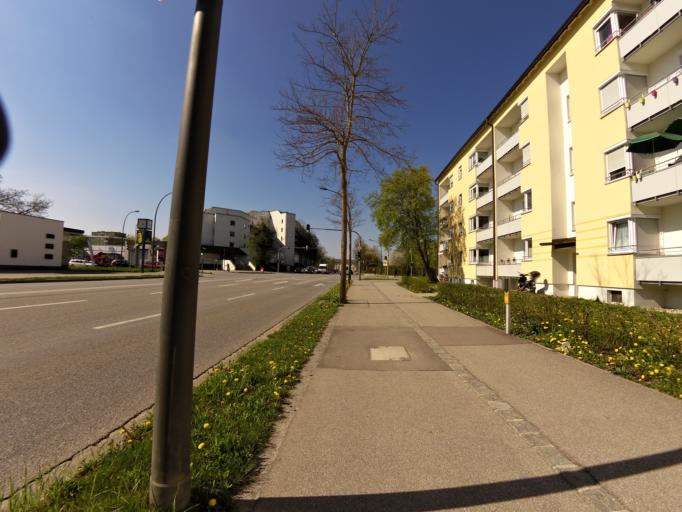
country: DE
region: Bavaria
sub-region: Lower Bavaria
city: Landshut
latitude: 48.5438
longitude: 12.1384
